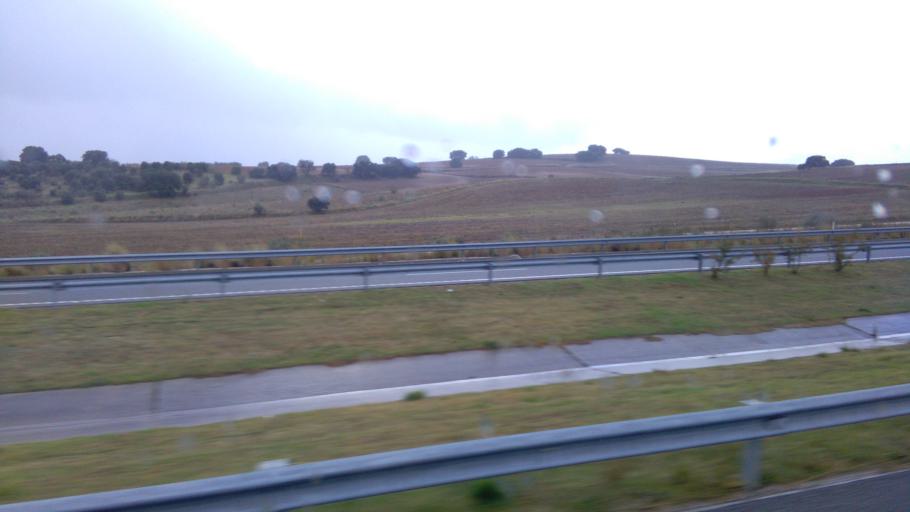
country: ES
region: Madrid
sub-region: Provincia de Madrid
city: El Alamo
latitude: 40.2621
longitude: -3.9672
